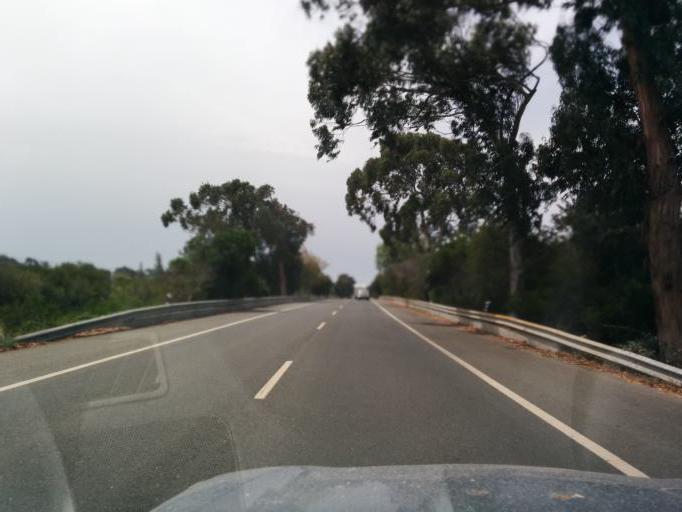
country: PT
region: Beja
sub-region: Odemira
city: Vila Nova de Milfontes
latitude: 37.7110
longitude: -8.7677
